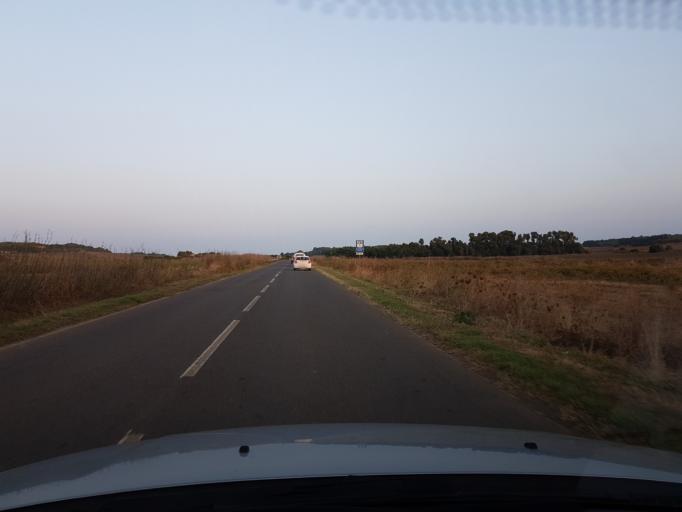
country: IT
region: Sardinia
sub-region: Provincia di Oristano
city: Cabras
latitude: 39.9447
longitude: 8.4346
